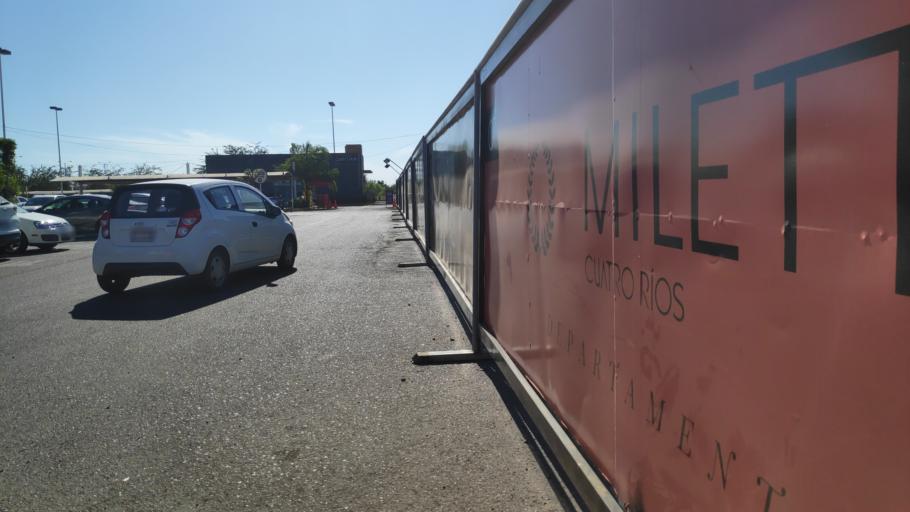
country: MX
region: Sinaloa
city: Culiacan
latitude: 24.8225
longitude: -107.4004
